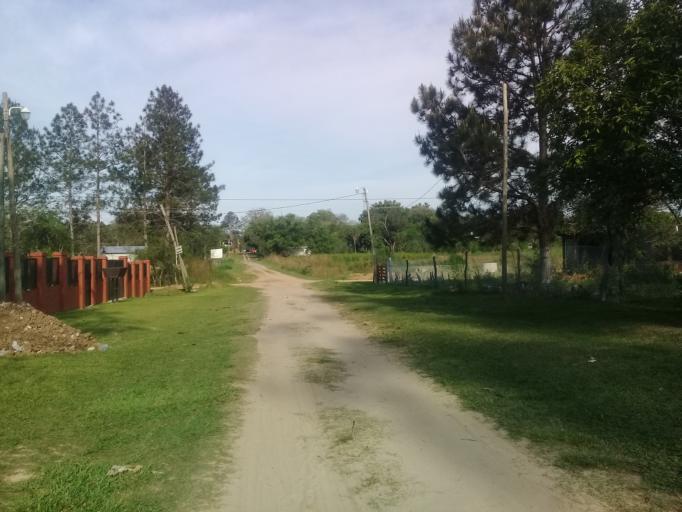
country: AR
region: Corrientes
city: San Luis del Palmar
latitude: -27.4542
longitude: -58.6583
